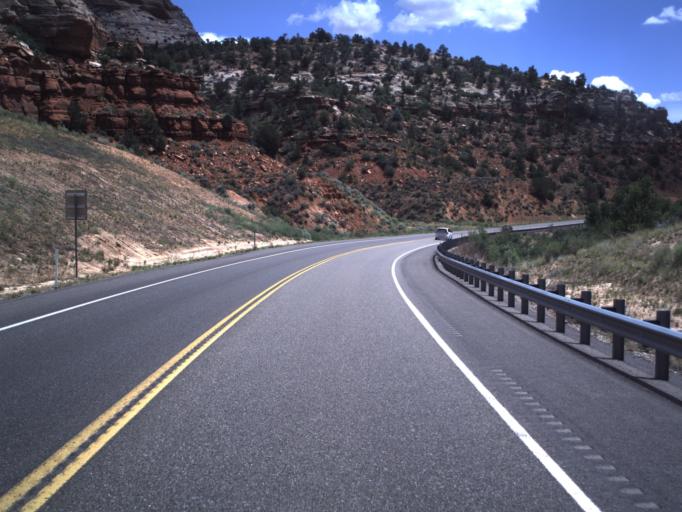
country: US
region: Utah
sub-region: Kane County
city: Kanab
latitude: 37.0971
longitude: -112.5450
